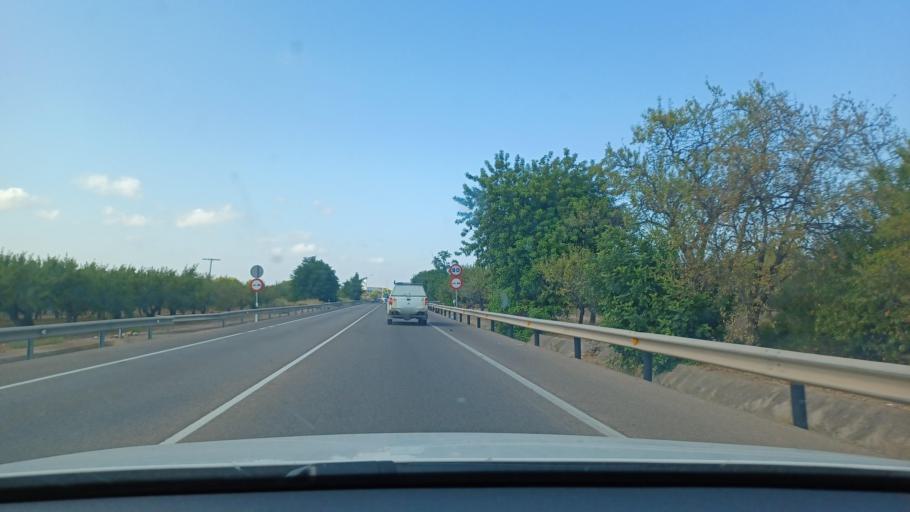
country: ES
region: Valencia
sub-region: Provincia de Castello
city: Orpesa/Oropesa del Mar
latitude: 40.1006
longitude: 0.1349
